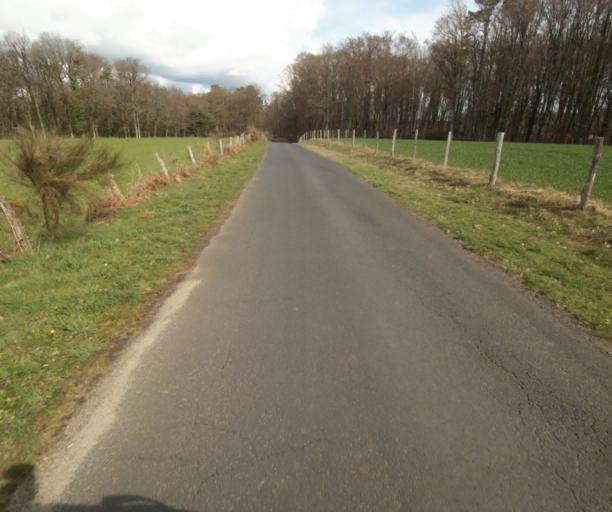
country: FR
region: Limousin
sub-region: Departement de la Correze
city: Correze
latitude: 45.3563
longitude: 1.8982
